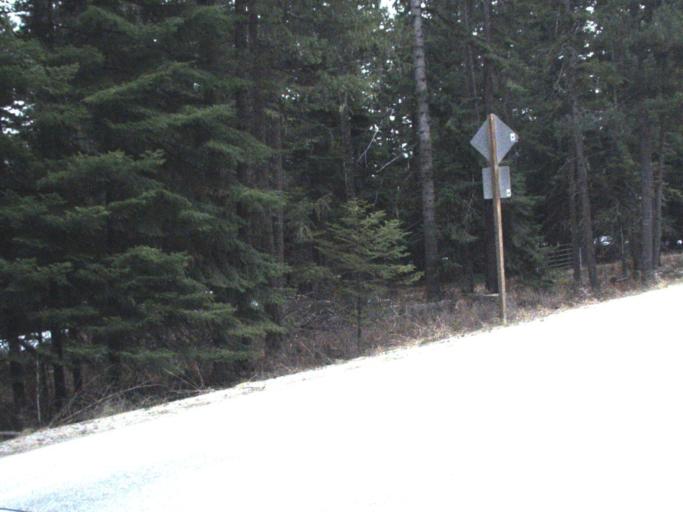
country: US
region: Washington
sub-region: Pend Oreille County
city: Newport
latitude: 48.2031
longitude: -117.0637
